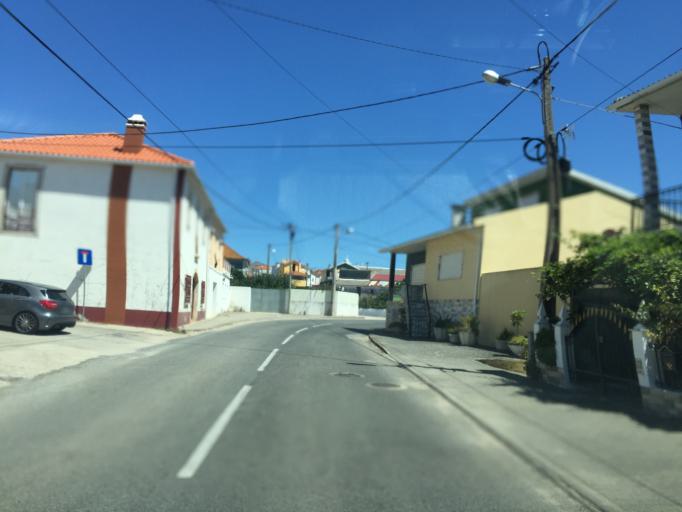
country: PT
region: Lisbon
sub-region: Torres Vedras
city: A dos Cunhados
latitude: 39.1885
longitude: -9.3046
